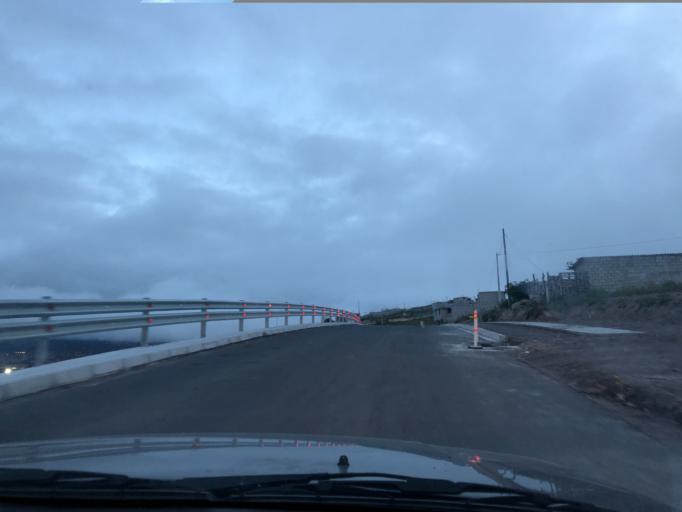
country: EC
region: Imbabura
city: Ibarra
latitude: 0.3747
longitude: -78.1272
